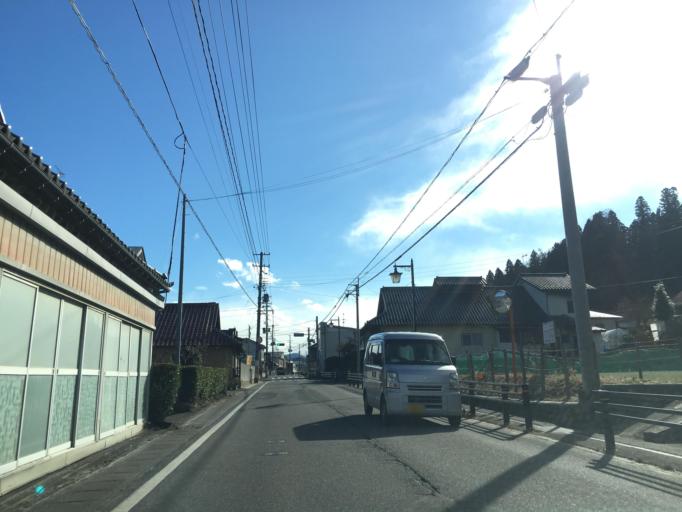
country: JP
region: Fukushima
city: Funehikimachi-funehiki
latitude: 37.3860
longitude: 140.6292
